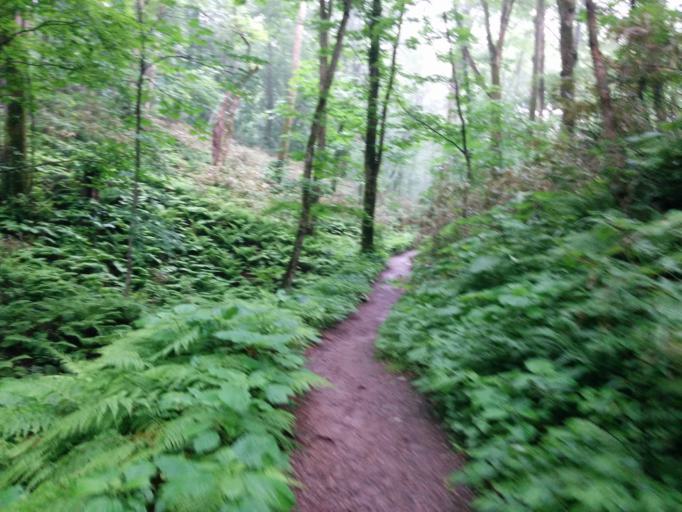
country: JP
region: Akita
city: Noshiromachi
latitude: 40.5626
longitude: 139.9801
